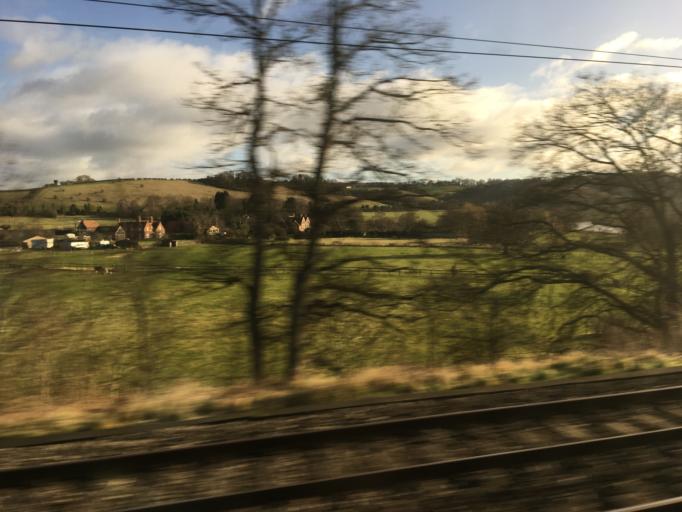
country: GB
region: England
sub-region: Oxfordshire
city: Goring
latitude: 51.5132
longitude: -1.1291
